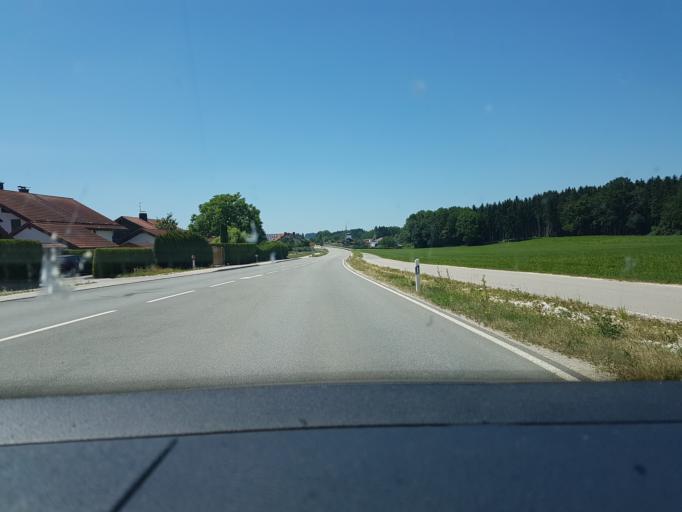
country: DE
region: Bavaria
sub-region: Upper Bavaria
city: Ainring
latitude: 47.8325
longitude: 12.9363
